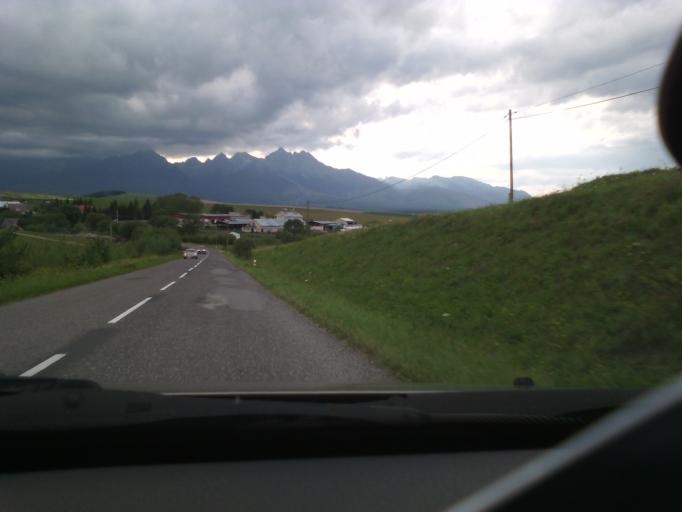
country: SK
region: Presovsky
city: Lubica
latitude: 49.0844
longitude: 20.4078
